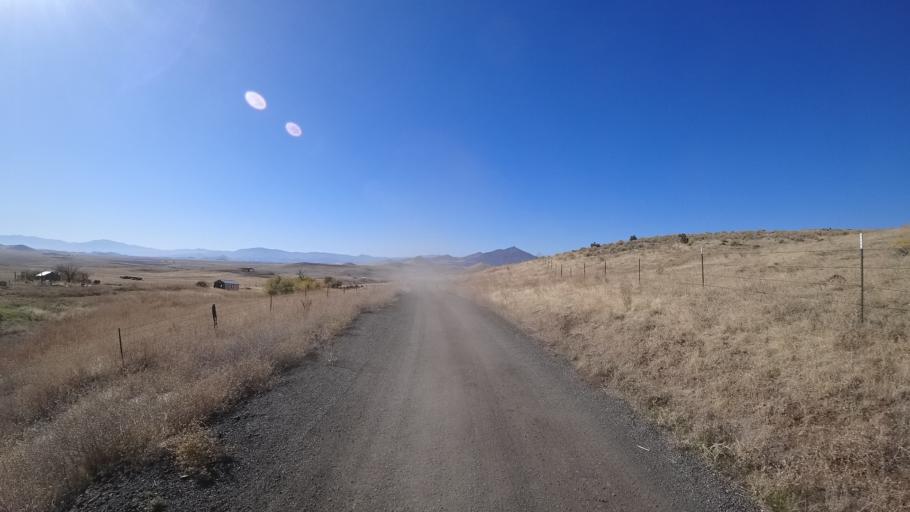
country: US
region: California
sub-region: Siskiyou County
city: Montague
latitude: 41.8446
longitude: -122.4210
